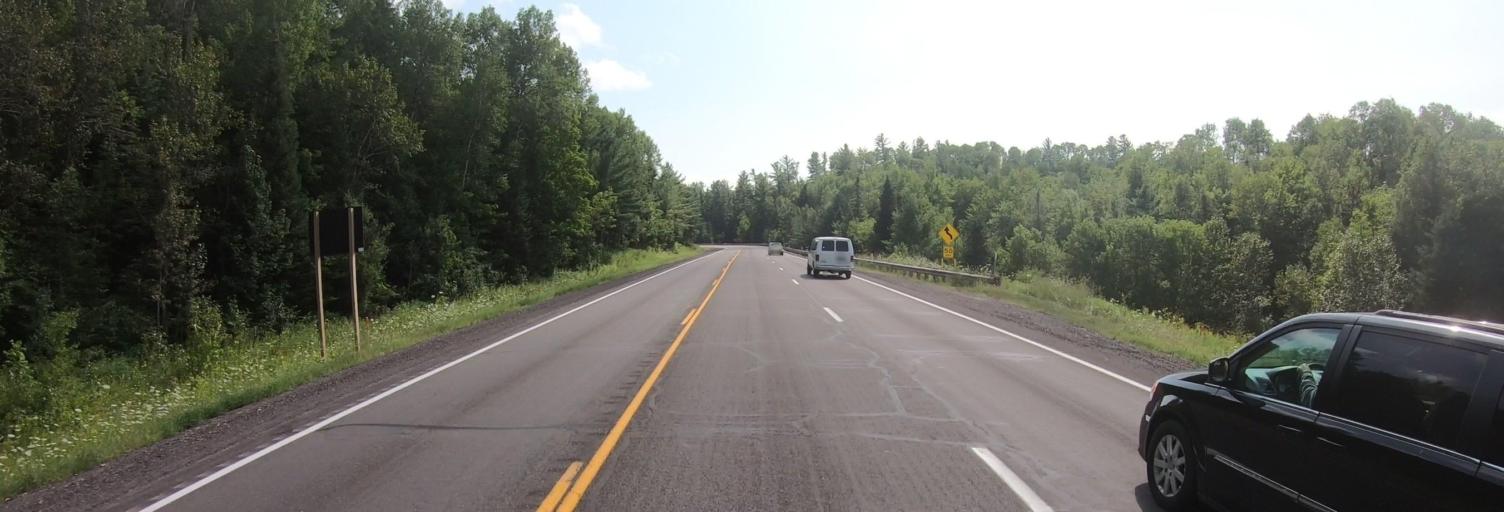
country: US
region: Michigan
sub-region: Ontonagon County
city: Ontonagon
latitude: 46.6944
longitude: -89.1642
